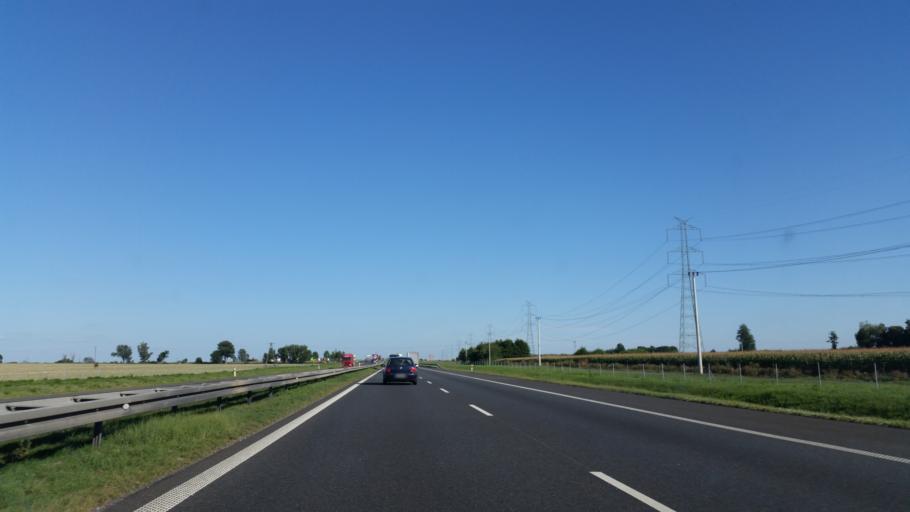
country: PL
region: Opole Voivodeship
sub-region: Powiat brzeski
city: Olszanka
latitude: 50.7609
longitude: 17.4217
